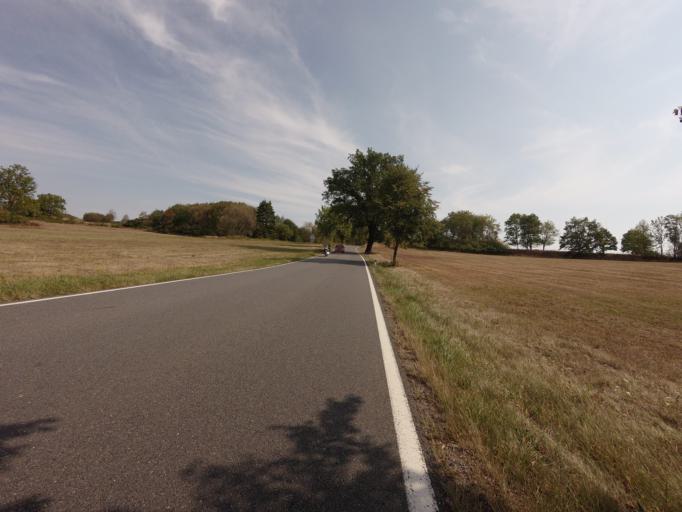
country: CZ
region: Central Bohemia
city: Petrovice
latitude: 49.5617
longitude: 14.3568
